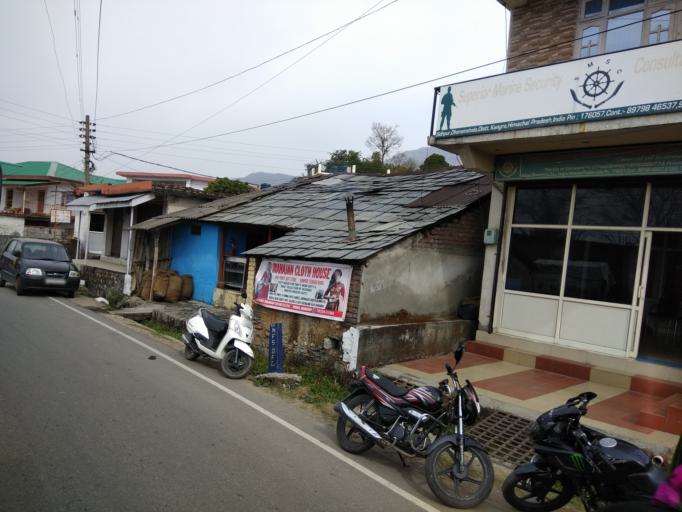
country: IN
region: Himachal Pradesh
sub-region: Kangra
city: Dharmsala
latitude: 32.1902
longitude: 76.3540
